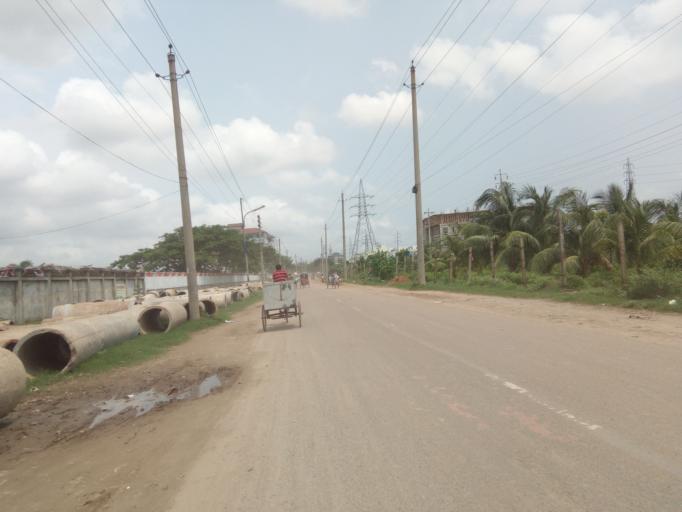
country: BD
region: Dhaka
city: Azimpur
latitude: 23.7269
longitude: 90.3679
